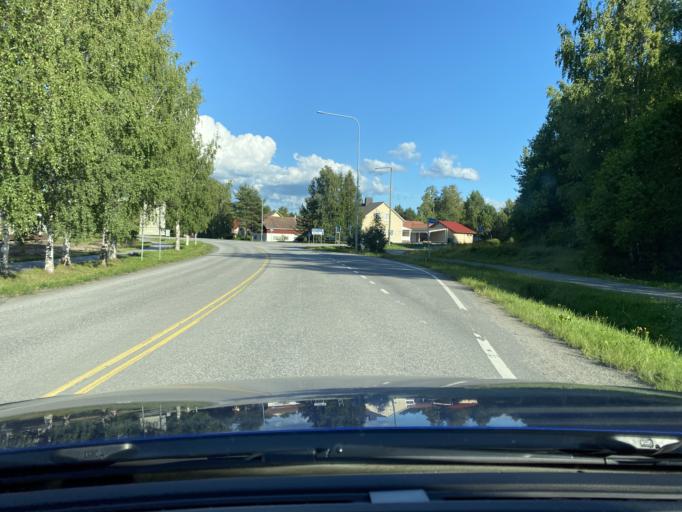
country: FI
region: Ostrobothnia
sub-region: Kyroenmaa
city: Laihia
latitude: 62.9763
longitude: 22.0046
